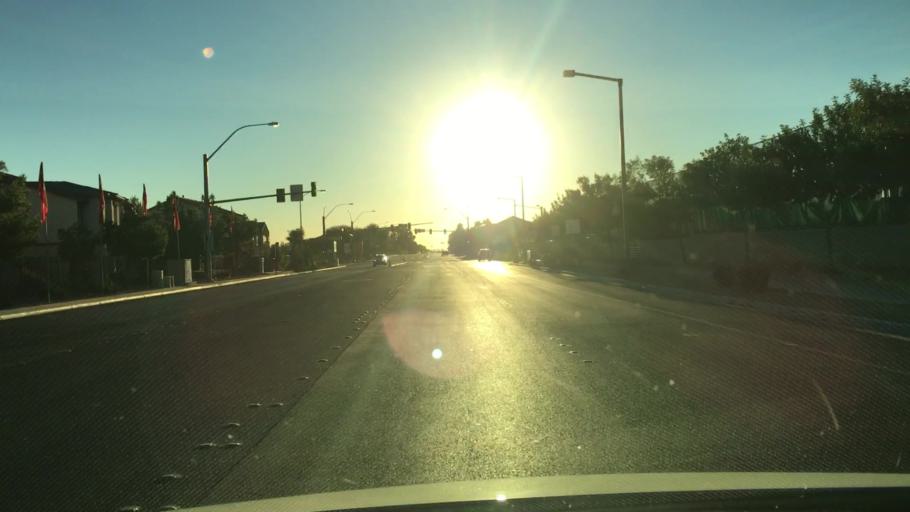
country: US
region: Nevada
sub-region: Clark County
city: Summerlin South
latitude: 36.0628
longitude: -115.2997
